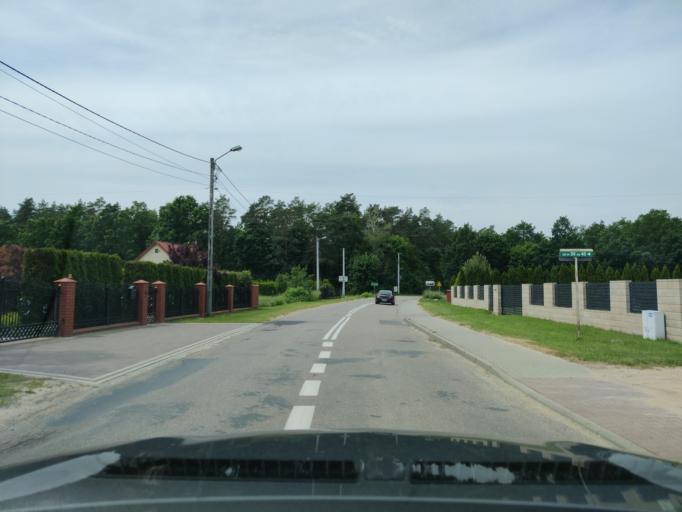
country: PL
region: Masovian Voivodeship
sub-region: Powiat wyszkowski
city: Rzasnik
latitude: 52.6989
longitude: 21.3997
